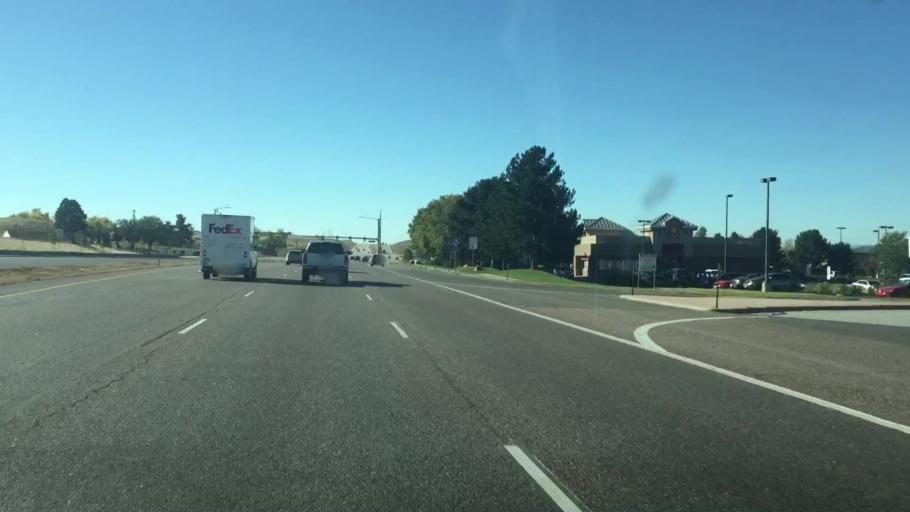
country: US
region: Colorado
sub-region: Douglas County
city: The Pinery
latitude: 39.4806
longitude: -104.7581
